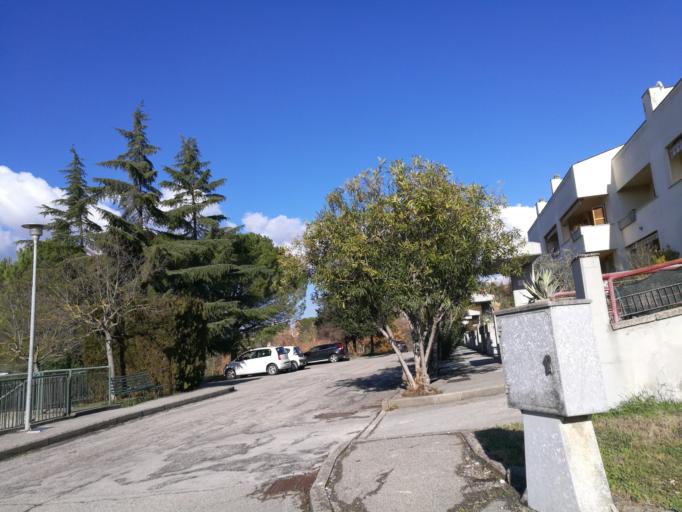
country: IT
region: Umbria
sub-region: Provincia di Perugia
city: Perugia
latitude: 43.0796
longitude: 12.3729
